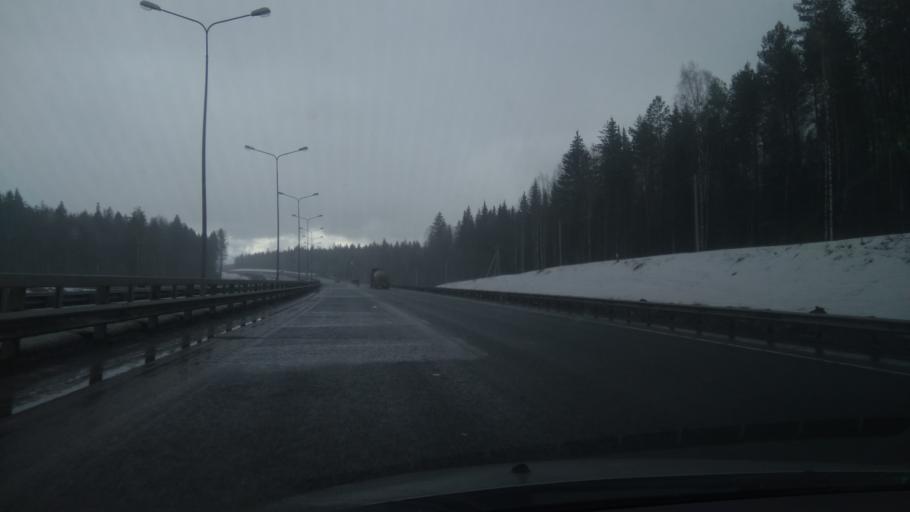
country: RU
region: Perm
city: Zvezdnyy
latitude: 57.7509
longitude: 56.3333
